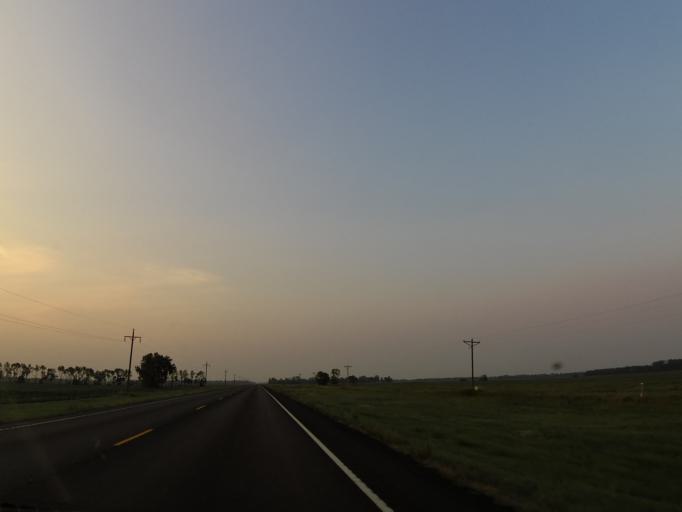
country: US
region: North Dakota
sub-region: Walsh County
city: Park River
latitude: 48.2710
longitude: -97.6225
